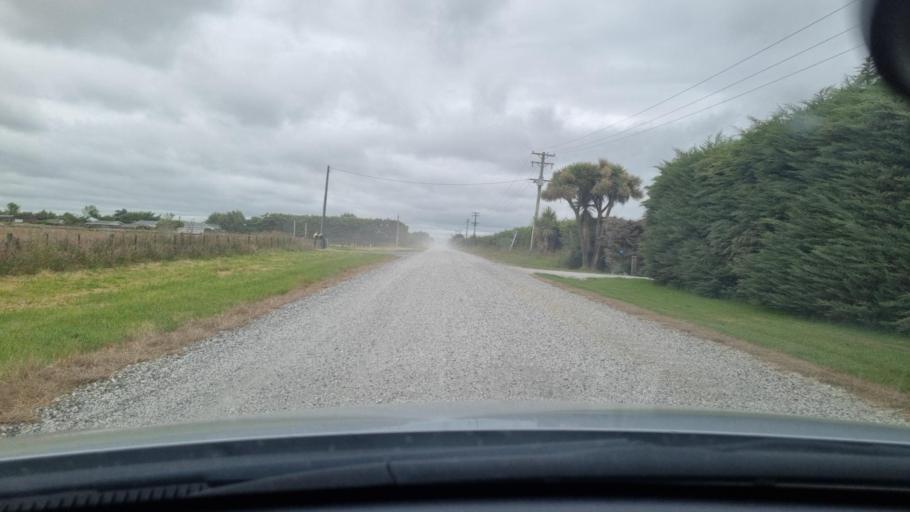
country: NZ
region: Southland
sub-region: Invercargill City
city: Invercargill
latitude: -46.3772
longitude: 168.2985
